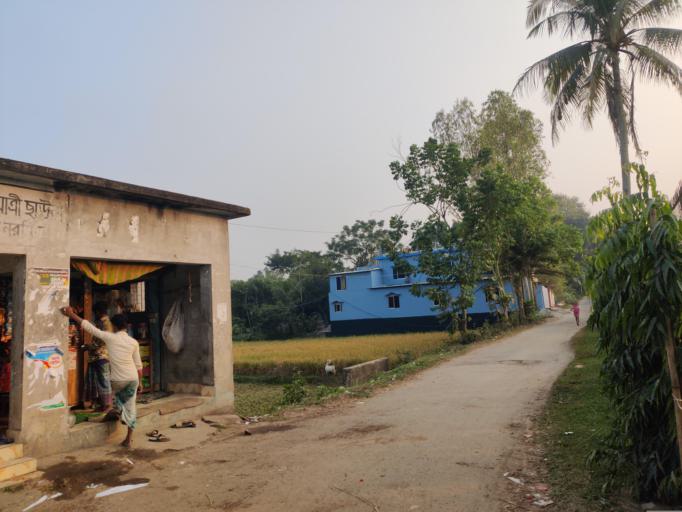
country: BD
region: Dhaka
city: Bajitpur
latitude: 24.1578
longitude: 90.7639
